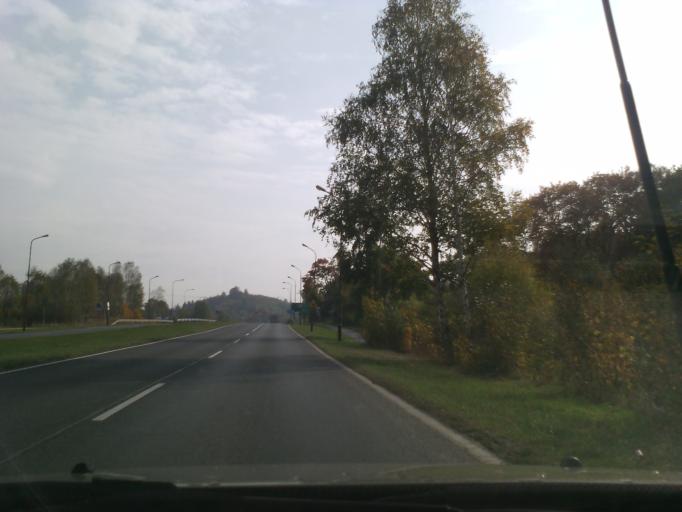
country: PL
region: Lower Silesian Voivodeship
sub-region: Powiat jeleniogorski
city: Jezow Sudecki
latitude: 50.9092
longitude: 15.7895
